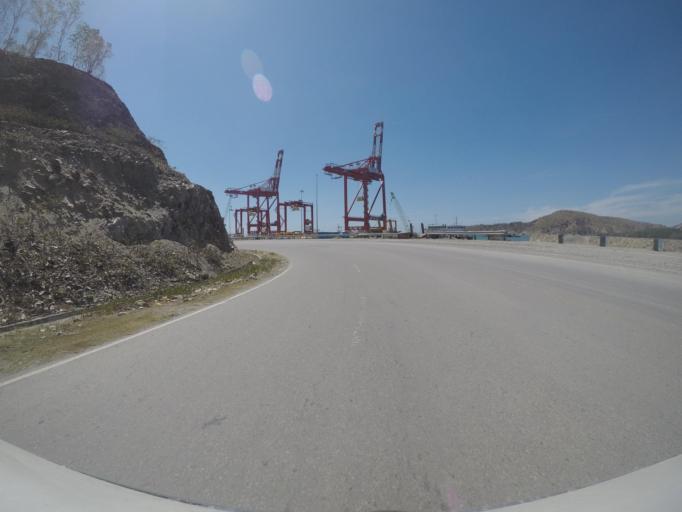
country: TL
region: Dili
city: Dili
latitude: -8.5743
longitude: 125.4777
